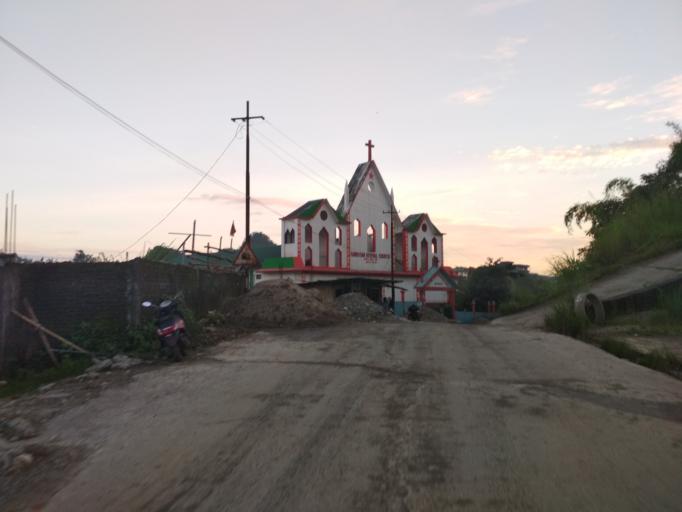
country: IN
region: Arunachal Pradesh
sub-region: Papum Pare
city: Naharlagun
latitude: 27.1002
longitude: 93.6712
